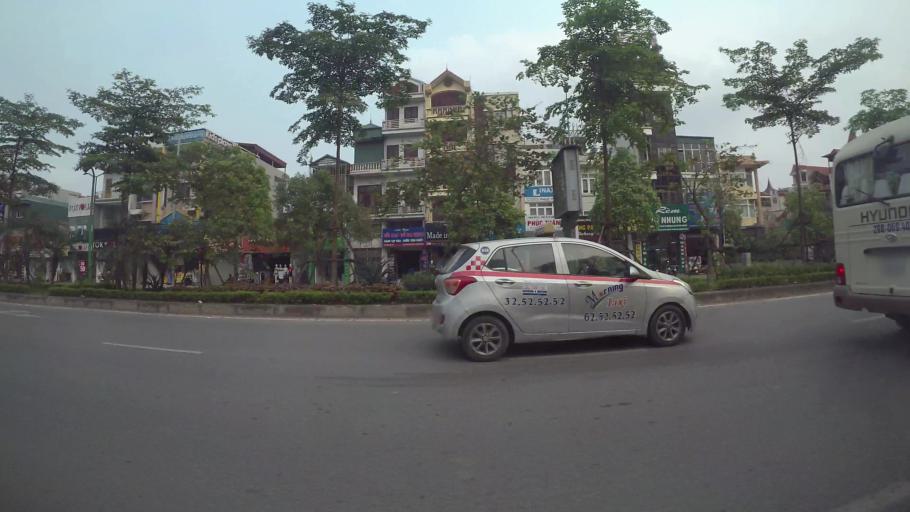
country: VN
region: Ha Noi
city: Hoan Kiem
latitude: 21.0608
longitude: 105.8933
